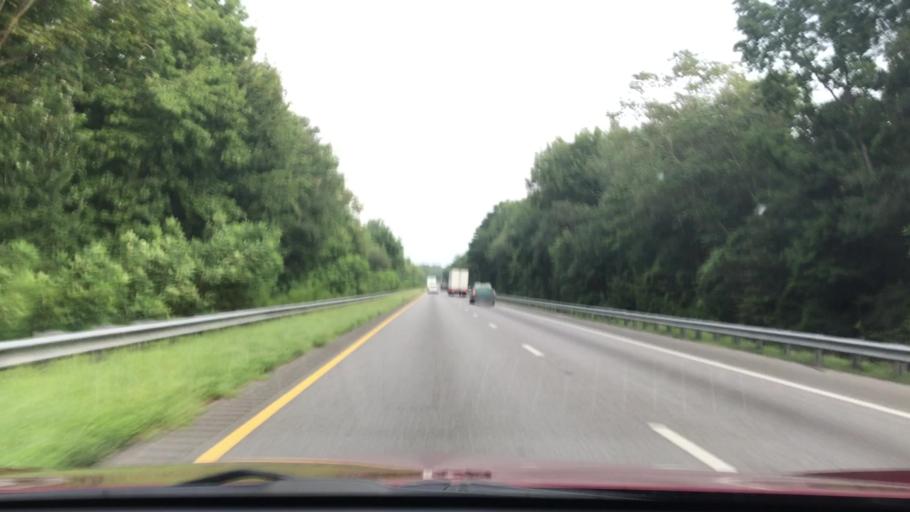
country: US
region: South Carolina
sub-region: Dorchester County
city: Ridgeville
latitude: 33.1488
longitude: -80.3342
